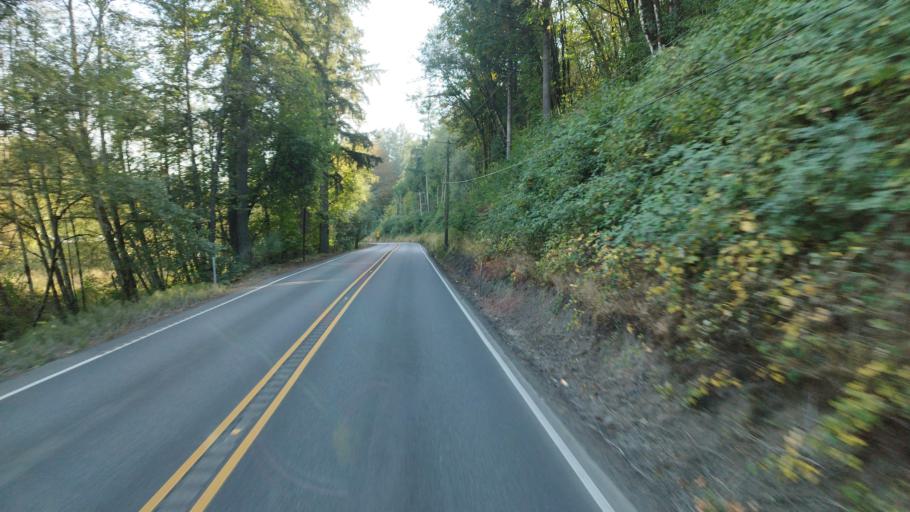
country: US
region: Oregon
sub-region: Washington County
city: Bethany
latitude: 45.6312
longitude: -122.8661
